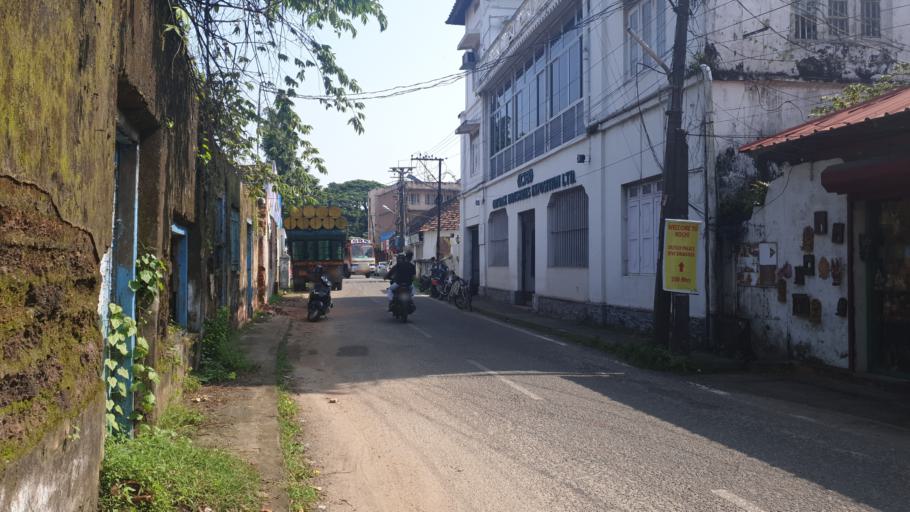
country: IN
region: Kerala
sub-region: Ernakulam
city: Cochin
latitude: 9.9612
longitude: 76.2589
